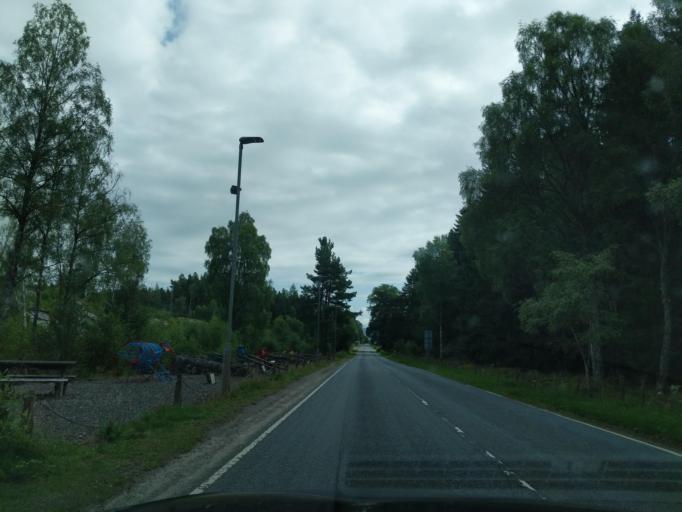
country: GB
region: Scotland
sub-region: Highland
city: Grantown on Spey
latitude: 57.3037
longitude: -3.6617
